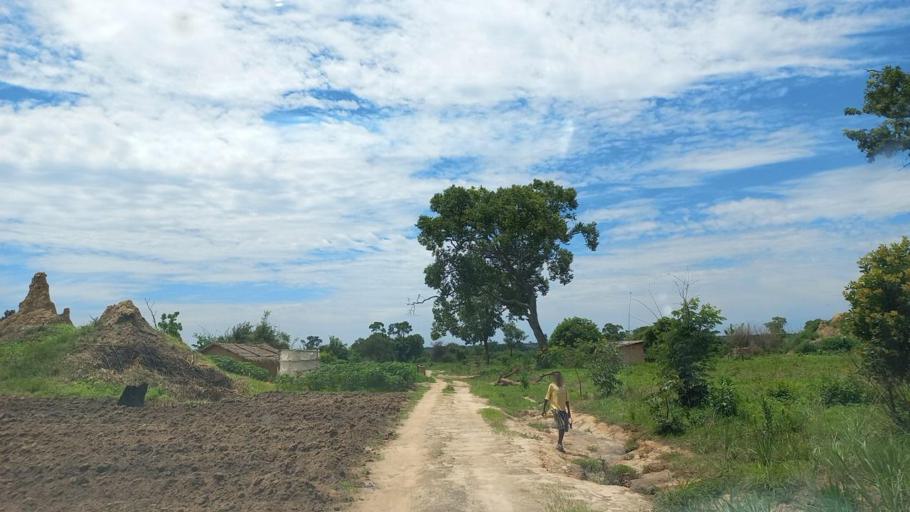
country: ZM
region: Copperbelt
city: Kitwe
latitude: -12.8049
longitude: 28.4011
